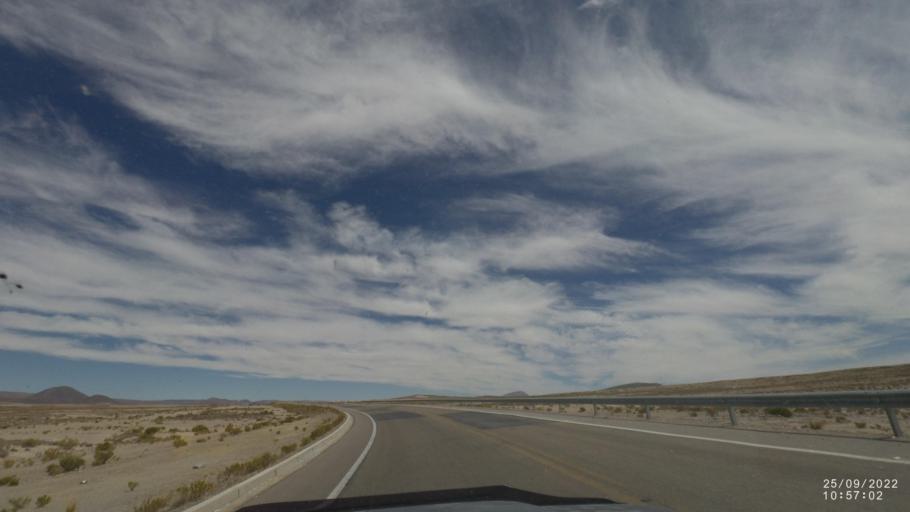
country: BO
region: Oruro
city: Challapata
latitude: -19.4775
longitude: -66.8845
